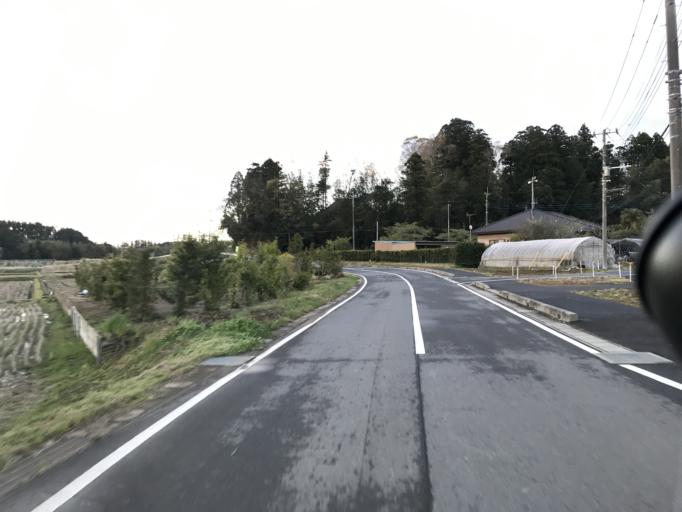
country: JP
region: Chiba
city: Sawara
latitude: 35.8163
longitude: 140.4923
